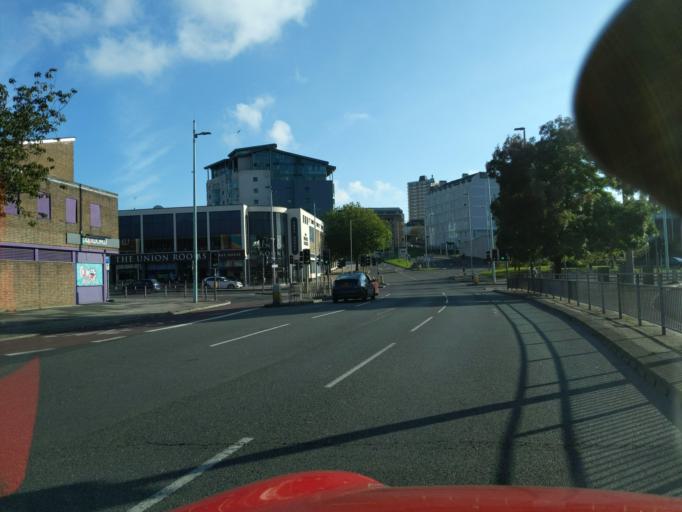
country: GB
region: England
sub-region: Plymouth
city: Plymouth
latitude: 50.3704
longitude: -4.1484
